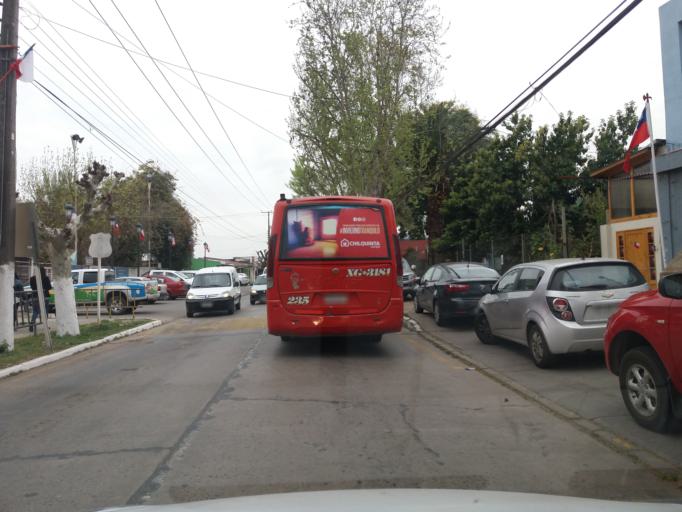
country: CL
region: Valparaiso
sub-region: Provincia de Quillota
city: Hacienda La Calera
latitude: -32.8019
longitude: -71.1446
